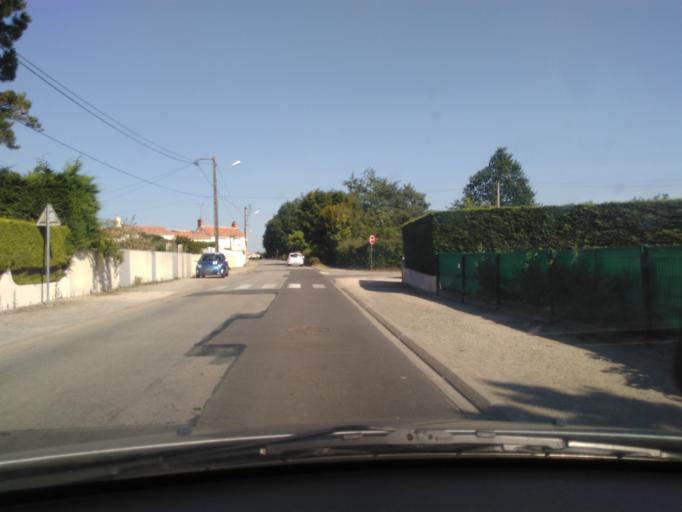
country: FR
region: Pays de la Loire
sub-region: Departement de la Vendee
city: Dompierre-sur-Yon
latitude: 46.7370
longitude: -1.3975
